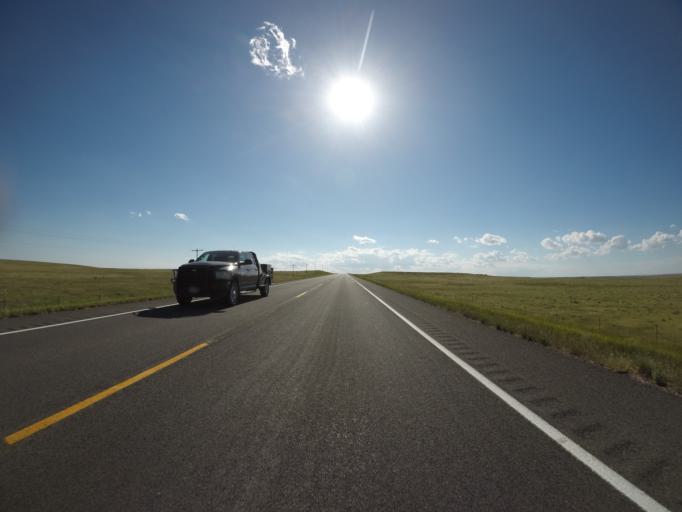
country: US
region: Colorado
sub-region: Morgan County
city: Brush
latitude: 40.6103
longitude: -103.6401
